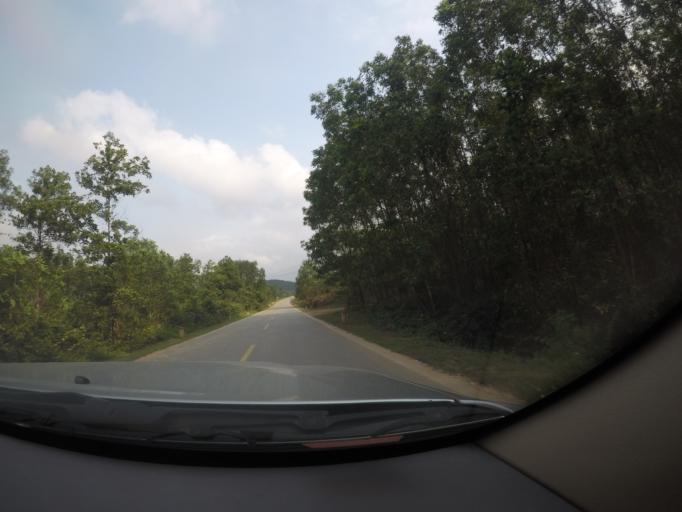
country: VN
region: Quang Binh
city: Kien Giang
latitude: 17.1144
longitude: 106.8339
